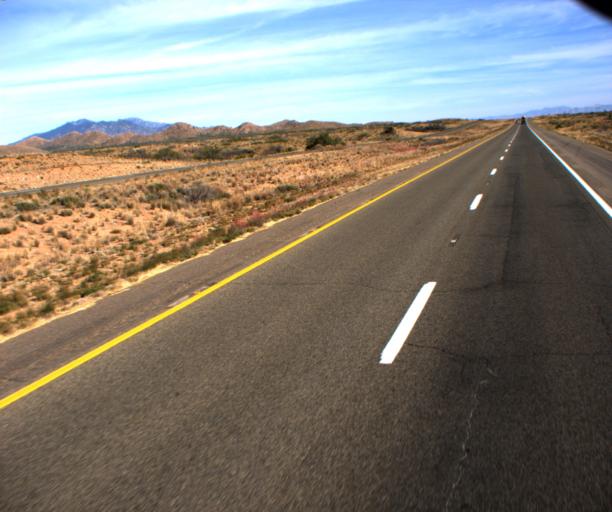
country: US
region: Arizona
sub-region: Graham County
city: Swift Trail Junction
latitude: 32.4794
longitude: -109.6728
